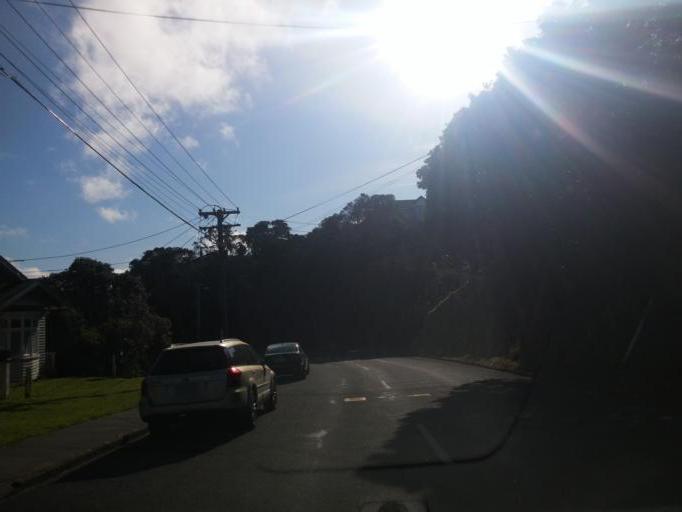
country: NZ
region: Wellington
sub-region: Wellington City
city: Brooklyn
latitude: -41.3133
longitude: 174.7642
